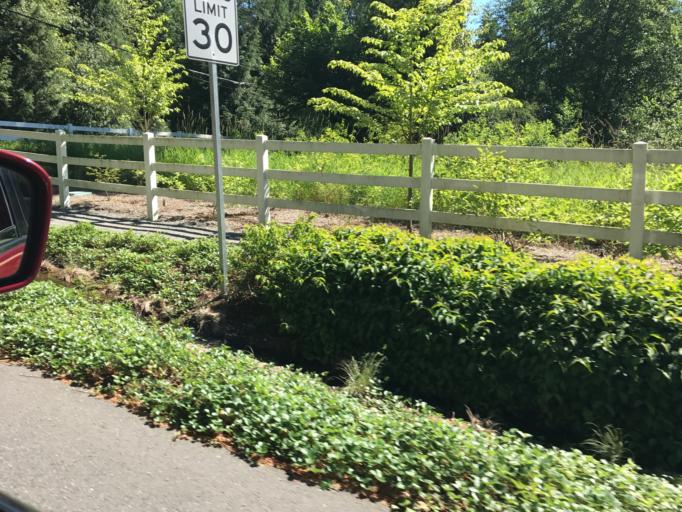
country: US
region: Washington
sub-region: King County
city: Bellevue
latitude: 47.6322
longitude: -122.1622
